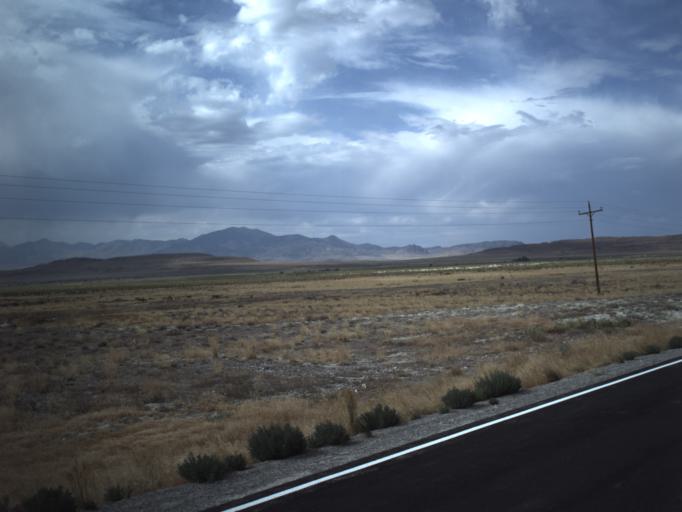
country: US
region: Utah
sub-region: Tooele County
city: Wendover
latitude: 41.4265
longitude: -113.8424
